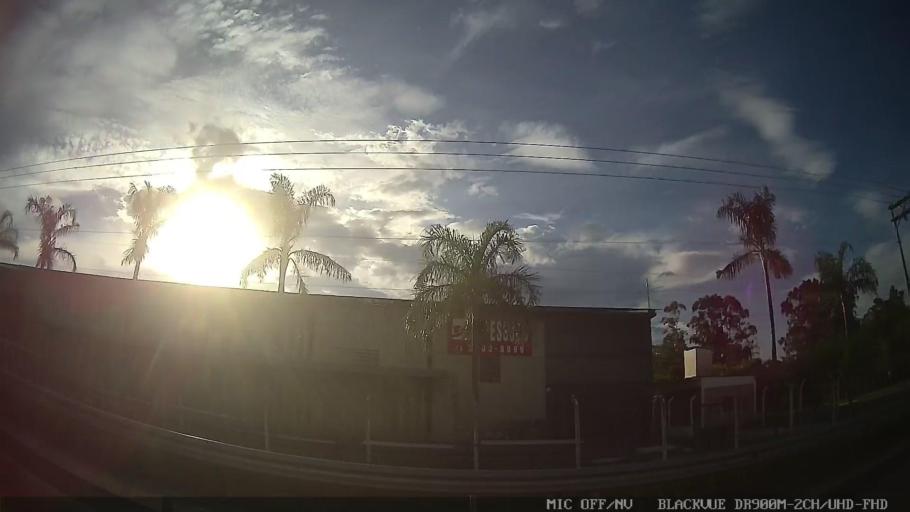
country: BR
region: Sao Paulo
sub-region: Tiete
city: Tiete
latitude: -23.0922
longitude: -47.7223
